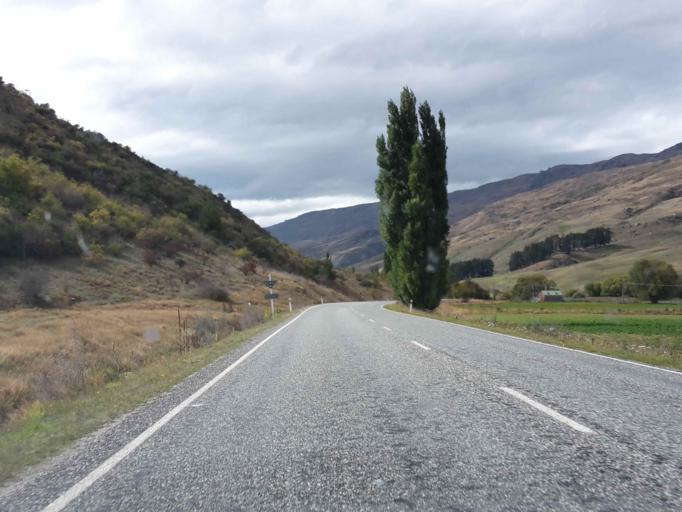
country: NZ
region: Otago
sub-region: Queenstown-Lakes District
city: Wanaka
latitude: -44.8515
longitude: 169.0380
